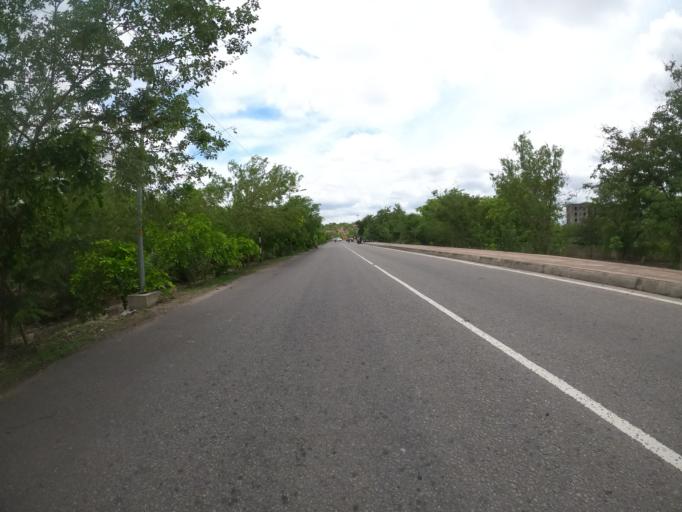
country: IN
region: Telangana
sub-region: Hyderabad
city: Hyderabad
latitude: 17.3718
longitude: 78.3501
